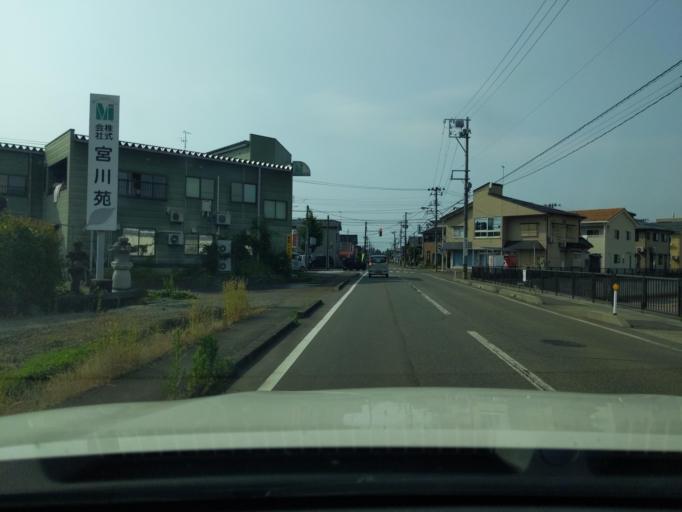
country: JP
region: Niigata
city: Nagaoka
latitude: 37.4295
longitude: 138.8606
